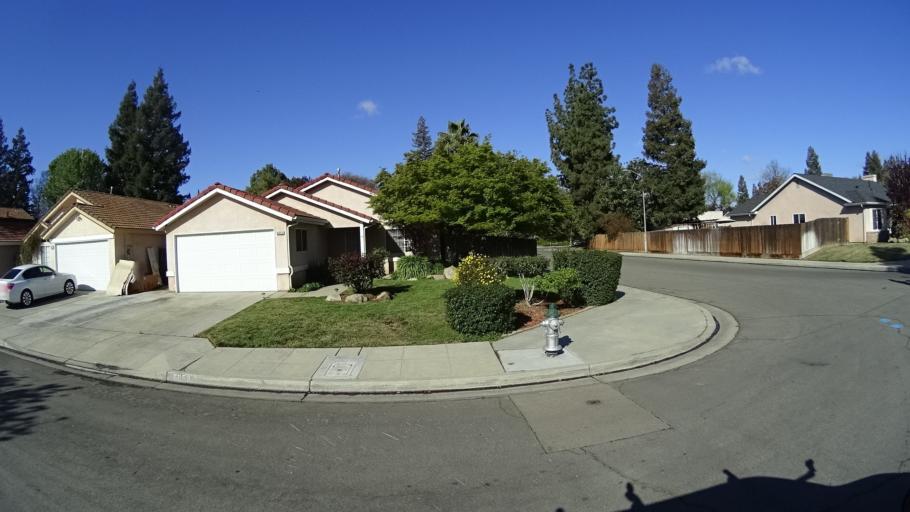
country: US
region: California
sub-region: Fresno County
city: West Park
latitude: 36.8233
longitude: -119.8735
